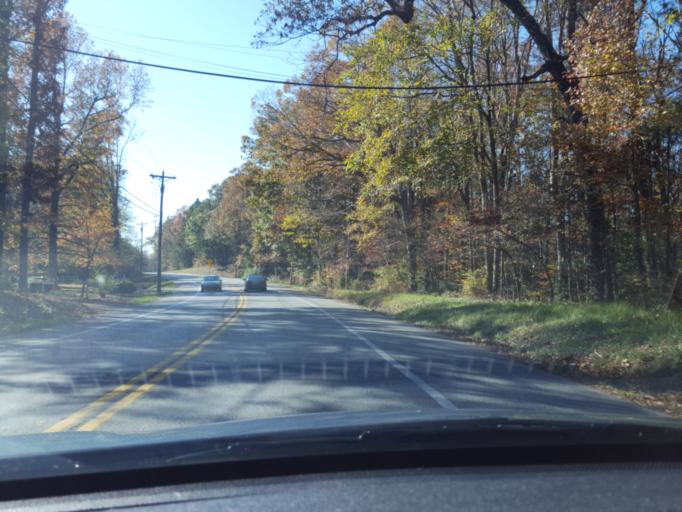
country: US
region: Maryland
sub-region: Saint Mary's County
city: California
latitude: 38.2864
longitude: -76.5529
